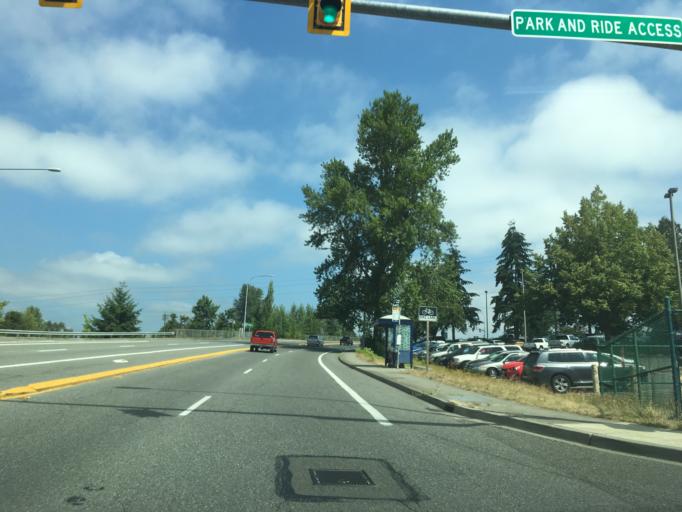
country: US
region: Washington
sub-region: King County
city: Kingsgate
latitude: 47.7404
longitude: -122.1892
